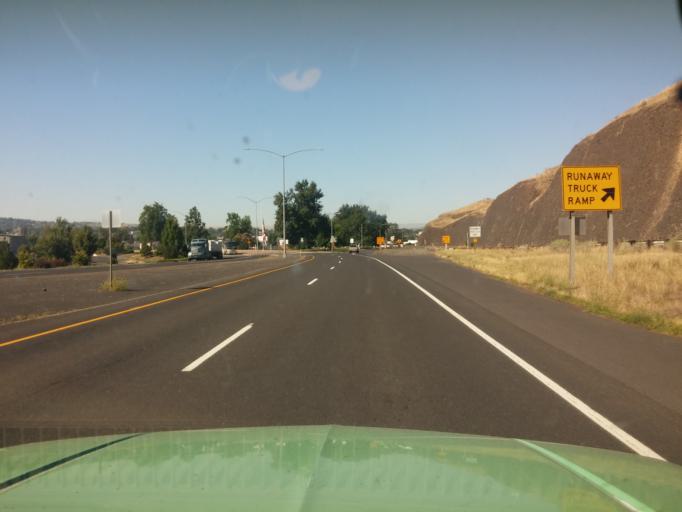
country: US
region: Idaho
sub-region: Nez Perce County
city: Lewiston
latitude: 46.4274
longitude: -116.9988
